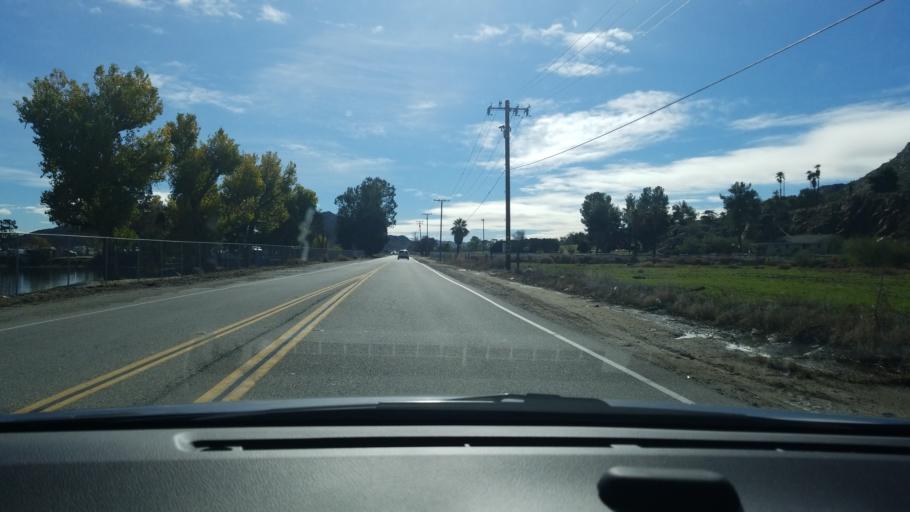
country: US
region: California
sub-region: Riverside County
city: Green Acres
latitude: 33.7857
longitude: -117.0336
